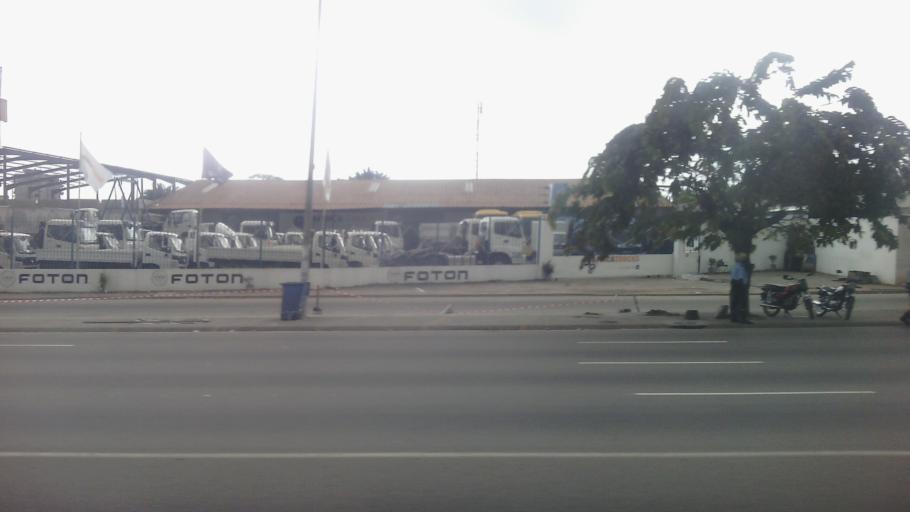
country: CI
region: Lagunes
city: Abidjan
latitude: 5.2977
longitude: -3.9843
